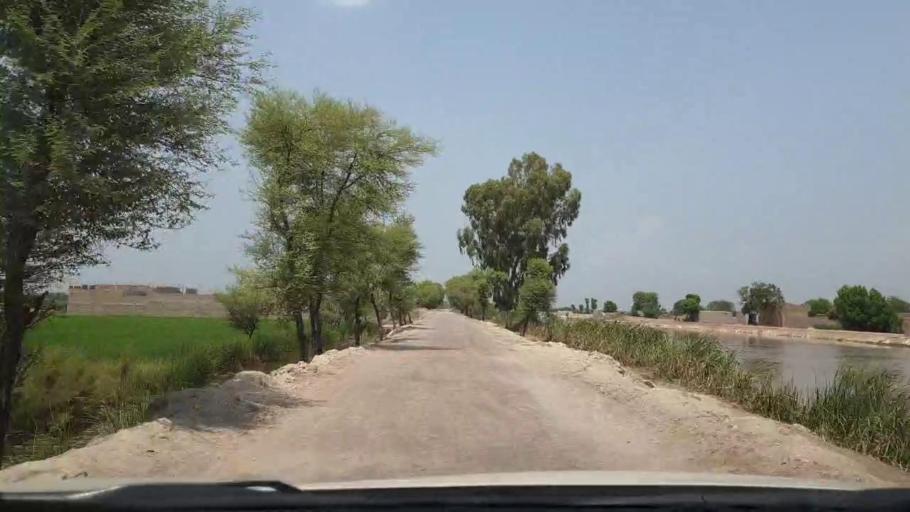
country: PK
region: Sindh
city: Dokri
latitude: 27.3357
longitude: 68.1102
